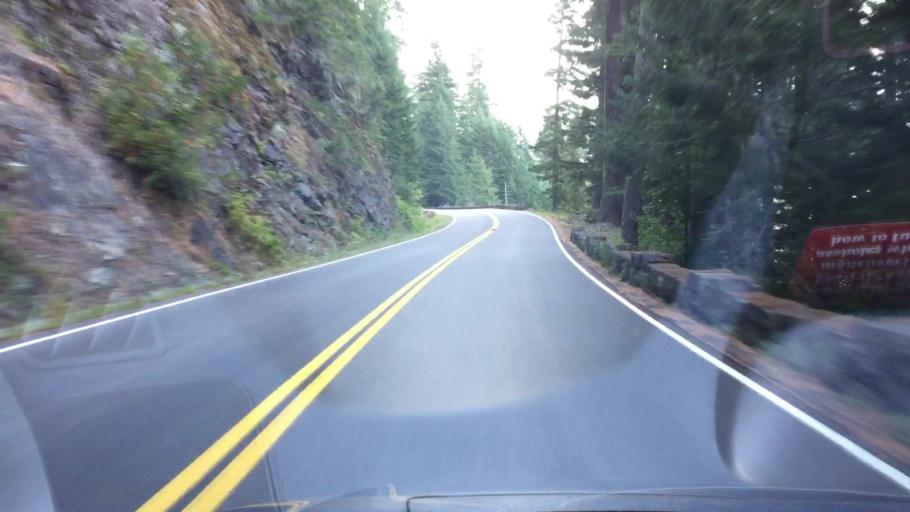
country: US
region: Washington
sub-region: Pierce County
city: Buckley
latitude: 46.7295
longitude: -121.5844
